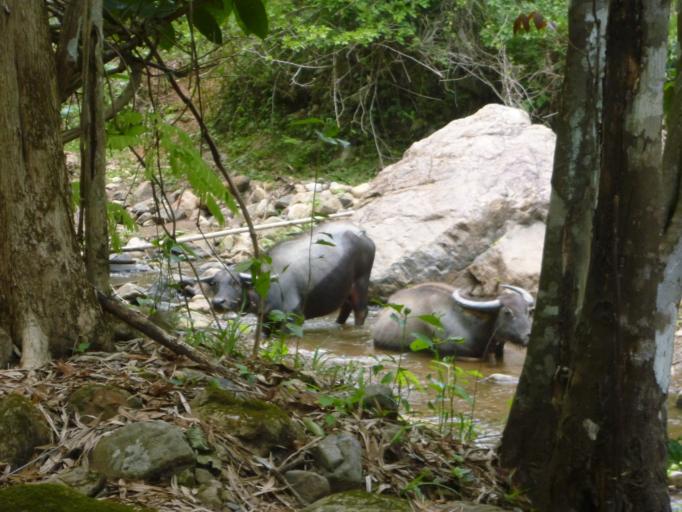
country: TH
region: Chiang Mai
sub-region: Amphoe Chiang Dao
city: Chiang Dao
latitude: 19.4682
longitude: 98.9068
